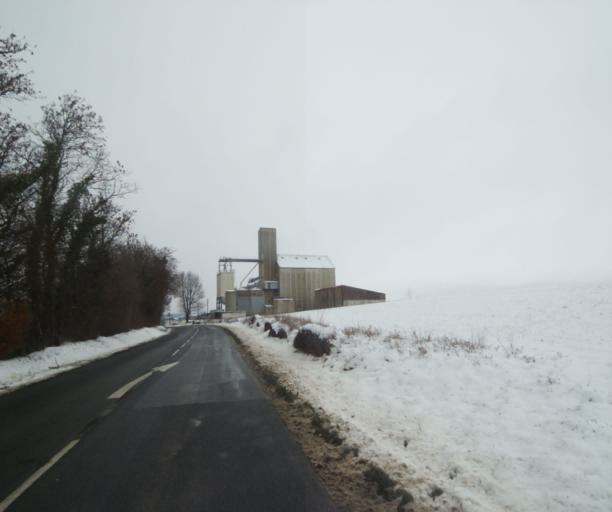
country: FR
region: Champagne-Ardenne
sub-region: Departement de la Haute-Marne
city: Wassy
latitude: 48.4326
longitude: 4.9620
